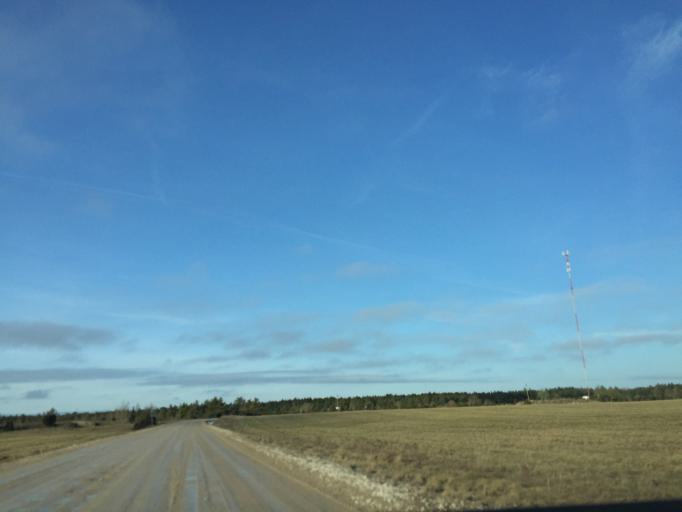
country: EE
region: Saare
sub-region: Kuressaare linn
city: Kuressaare
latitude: 58.4652
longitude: 22.0048
